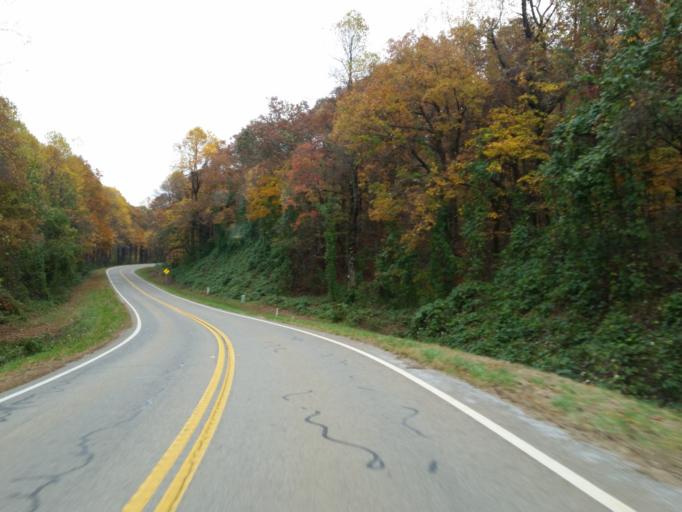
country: US
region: Georgia
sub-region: Pickens County
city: Jasper
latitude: 34.5420
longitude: -84.3548
